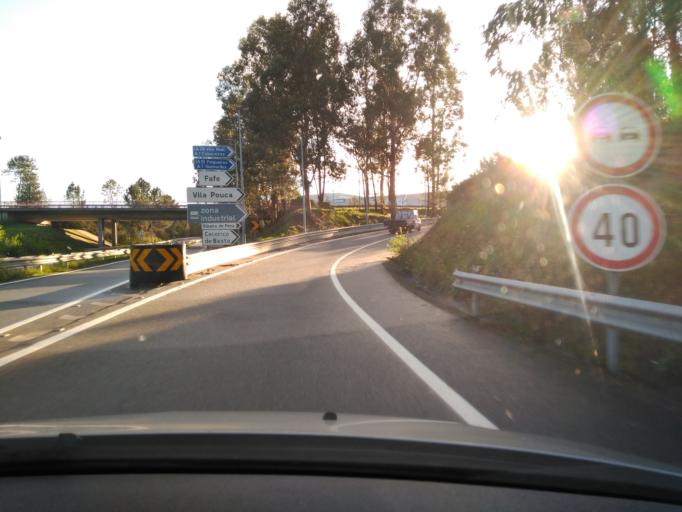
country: PT
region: Braga
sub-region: Fafe
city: Fafe
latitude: 41.4574
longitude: -8.1438
